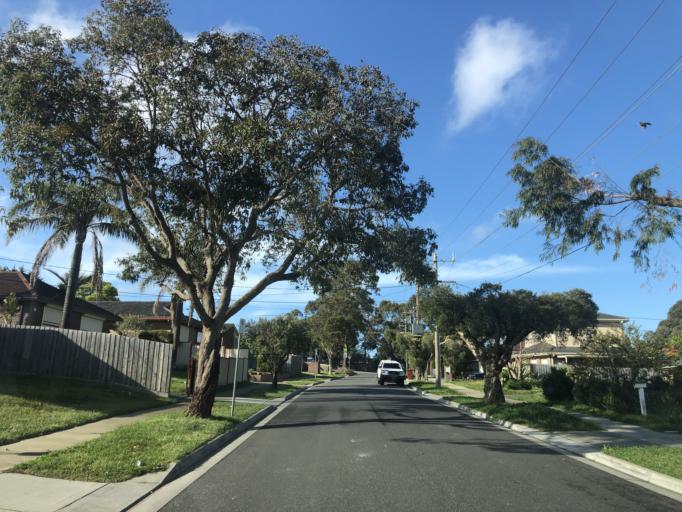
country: AU
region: Victoria
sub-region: Casey
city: Eumemmerring
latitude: -37.9992
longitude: 145.2620
